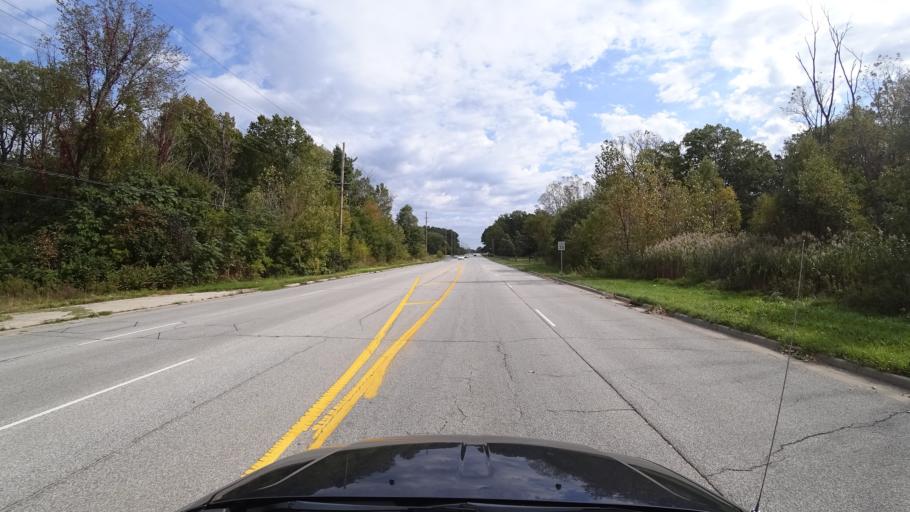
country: US
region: Indiana
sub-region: LaPorte County
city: Trail Creek
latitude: 41.6658
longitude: -86.8833
